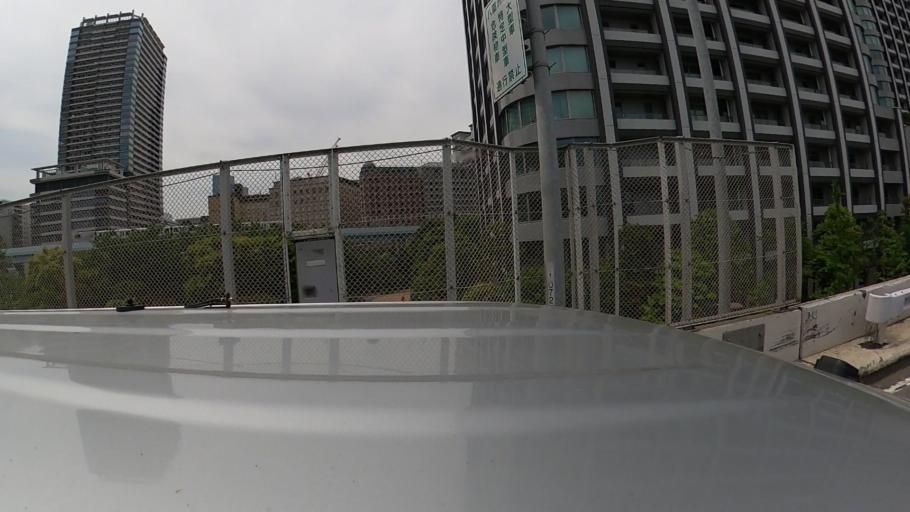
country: JP
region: Tokyo
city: Tokyo
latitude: 35.6600
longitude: 139.7600
